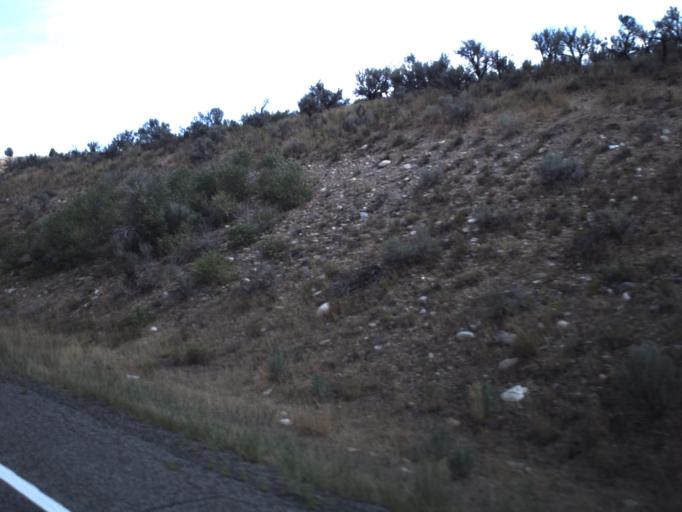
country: US
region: Utah
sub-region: Utah County
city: Woodland Hills
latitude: 39.9428
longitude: -111.5407
